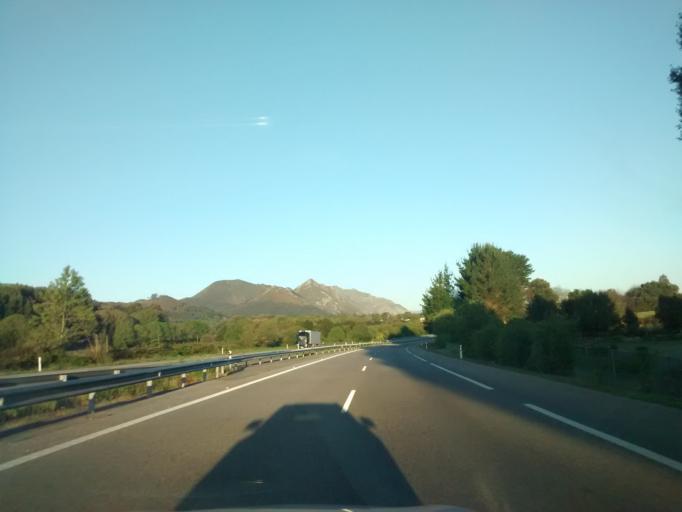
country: ES
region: Asturias
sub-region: Province of Asturias
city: Carrena
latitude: 43.4438
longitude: -4.9046
